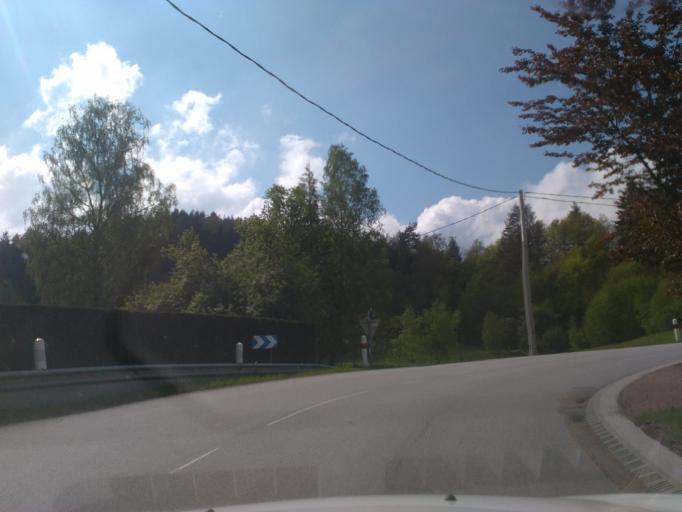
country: FR
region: Lorraine
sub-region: Departement des Vosges
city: Vagney
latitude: 47.9974
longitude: 6.7341
